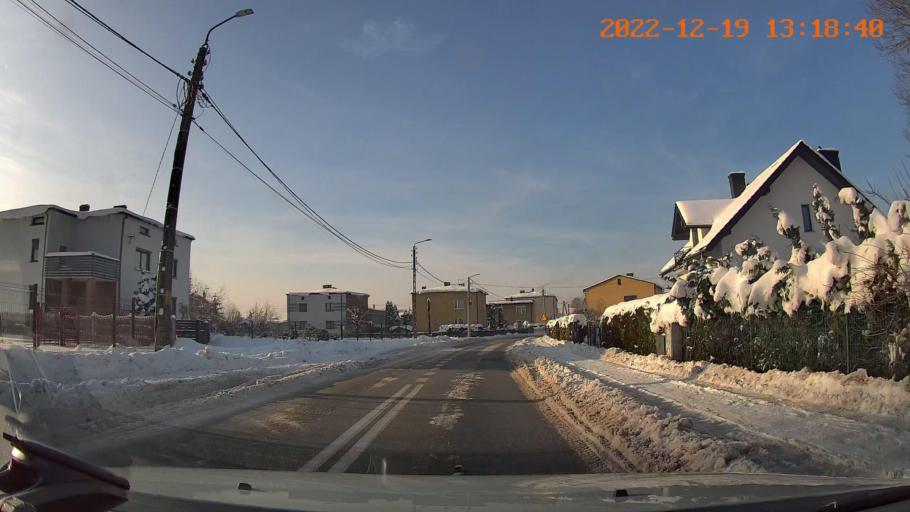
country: PL
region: Silesian Voivodeship
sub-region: Powiat bierunsko-ledzinski
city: Chelm Slaski
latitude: 50.1065
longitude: 19.1960
